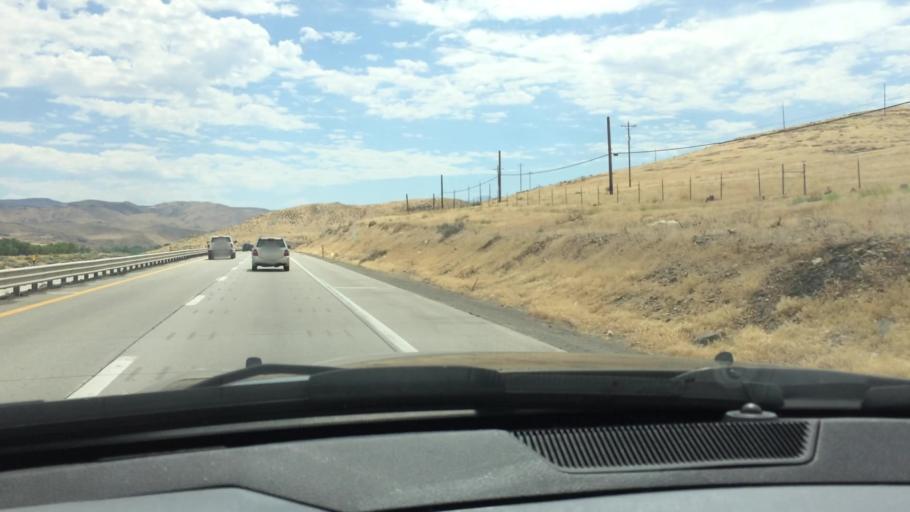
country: US
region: Nevada
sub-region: Washoe County
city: Sparks
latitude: 39.5351
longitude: -119.6039
